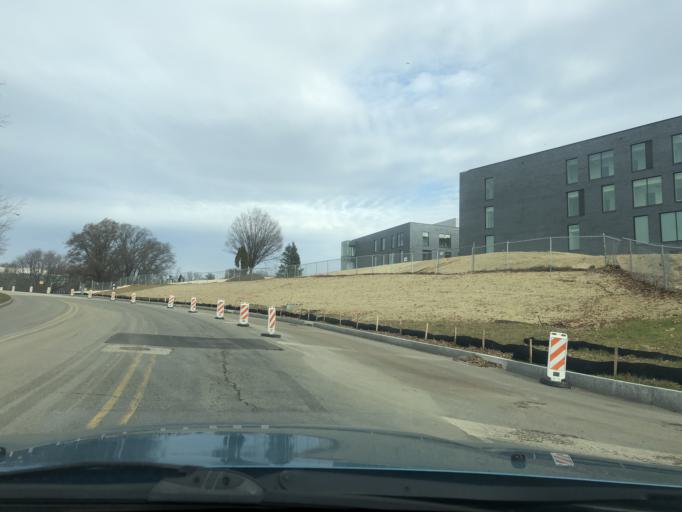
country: US
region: Pennsylvania
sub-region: Delaware County
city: Radnor
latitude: 40.0385
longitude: -75.3555
